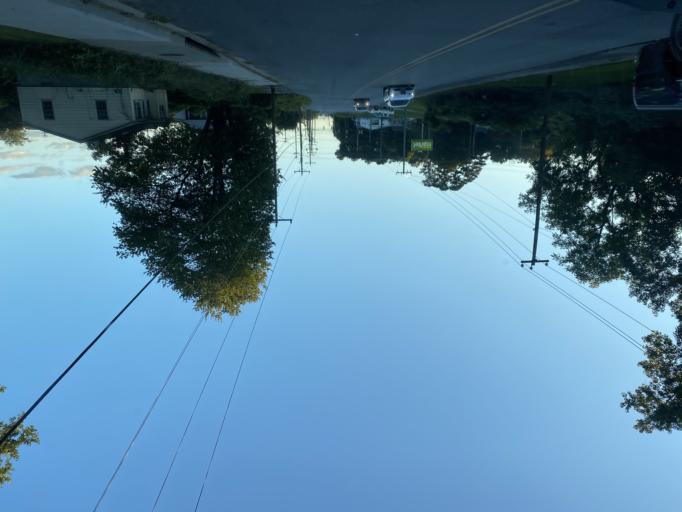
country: US
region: South Carolina
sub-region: Cherokee County
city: East Gaffney
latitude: 35.0823
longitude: -81.6389
